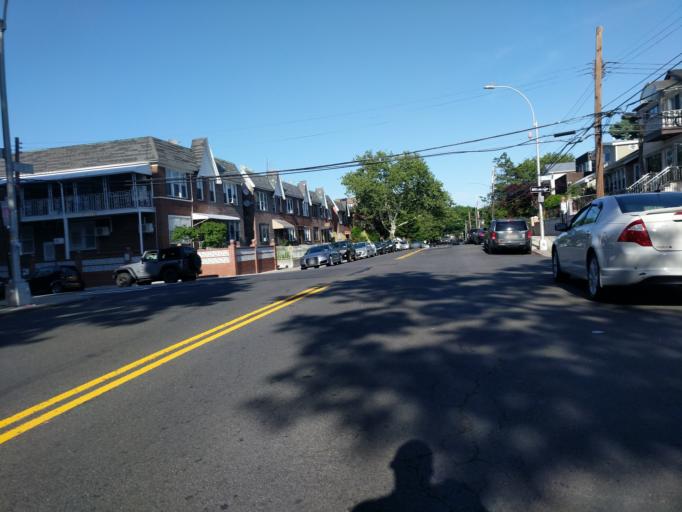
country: US
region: New York
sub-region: Queens County
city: Long Island City
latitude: 40.7382
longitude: -73.9267
